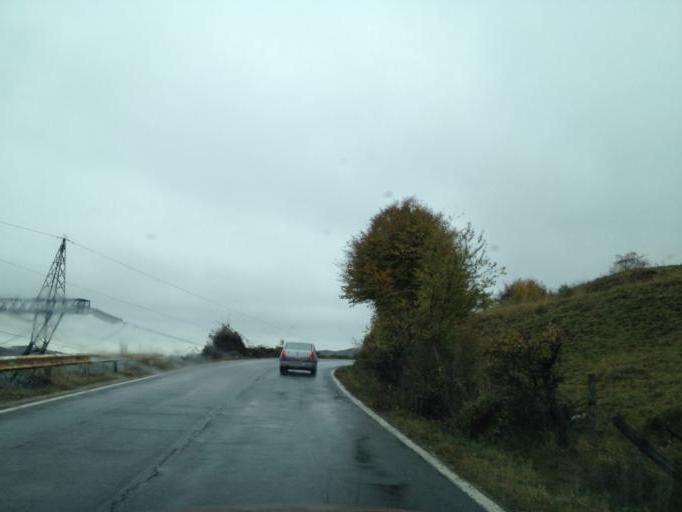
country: RO
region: Arges
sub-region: Comuna Dragoslavele
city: Dragoslavele
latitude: 45.2998
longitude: 25.1524
